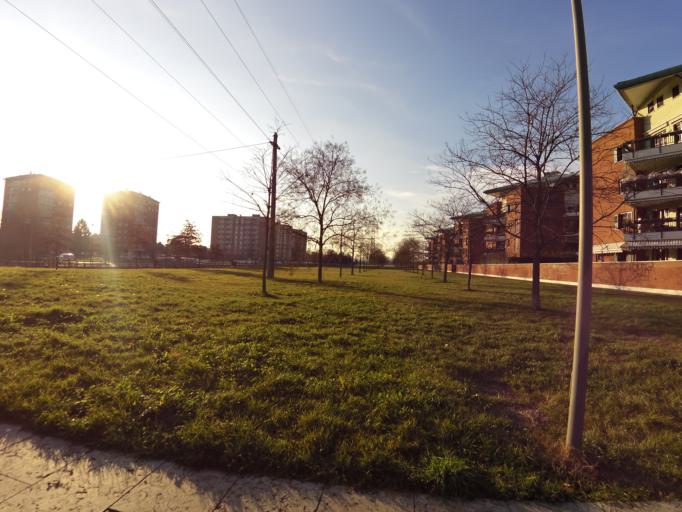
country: IT
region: Lombardy
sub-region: Citta metropolitana di Milano
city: Vimodrone
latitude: 45.5176
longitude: 9.2795
